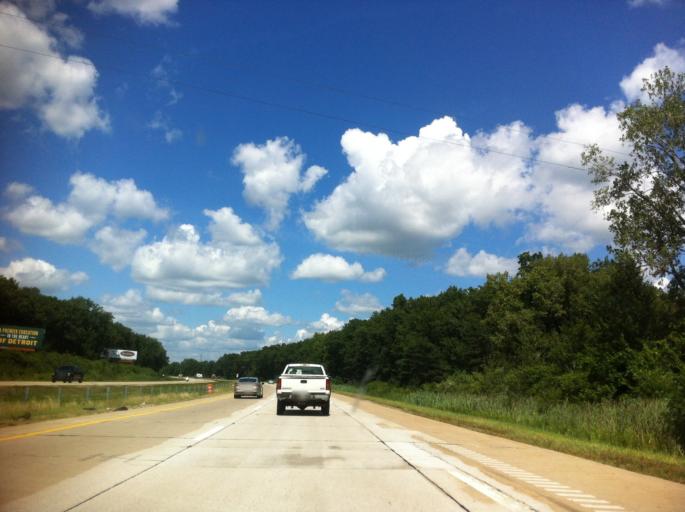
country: US
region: Michigan
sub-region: Monroe County
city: Petersburg
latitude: 41.8470
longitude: -83.6660
